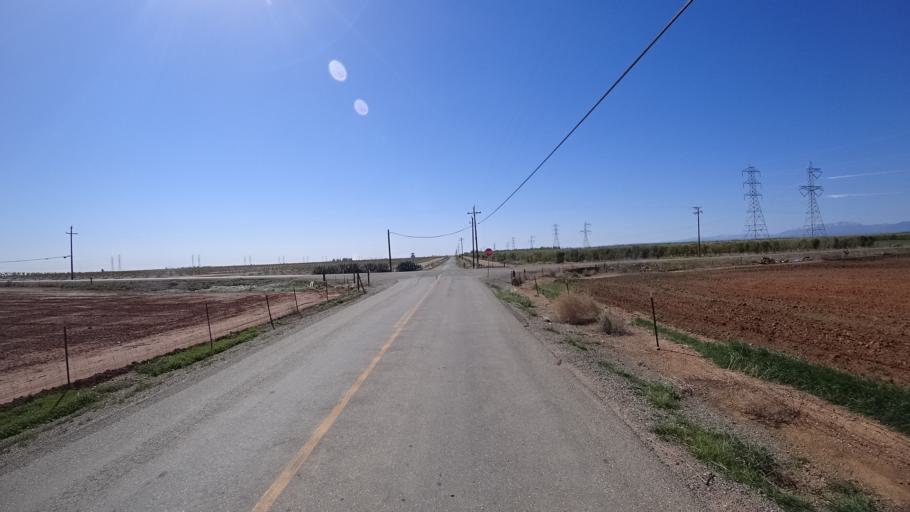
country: US
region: California
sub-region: Glenn County
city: Orland
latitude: 39.6690
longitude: -122.2719
